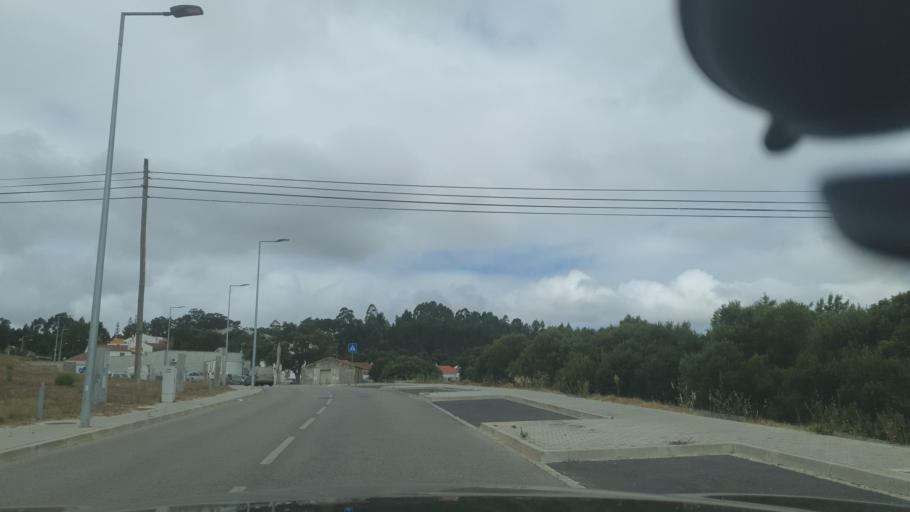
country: PT
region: Beja
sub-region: Odemira
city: Sao Teotonio
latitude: 37.5098
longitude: -8.7044
